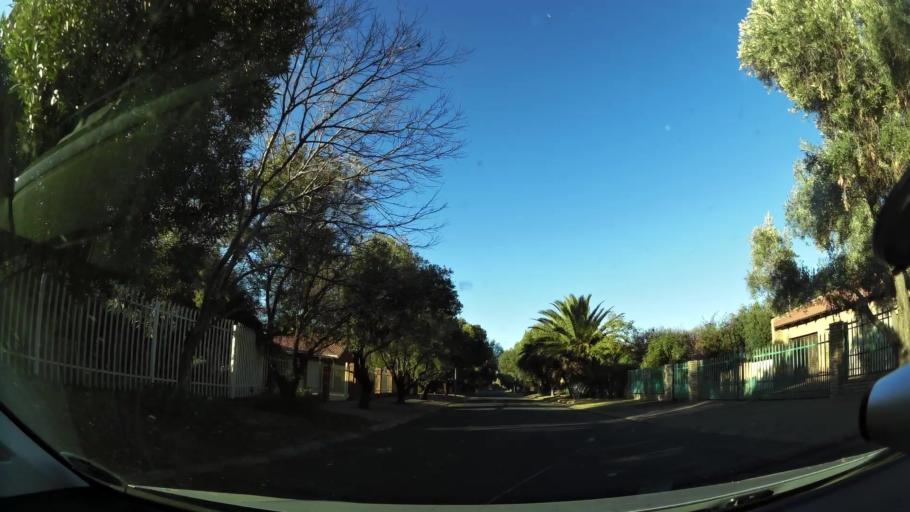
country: ZA
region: Northern Cape
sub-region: Frances Baard District Municipality
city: Kimberley
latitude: -28.7573
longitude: 24.7525
